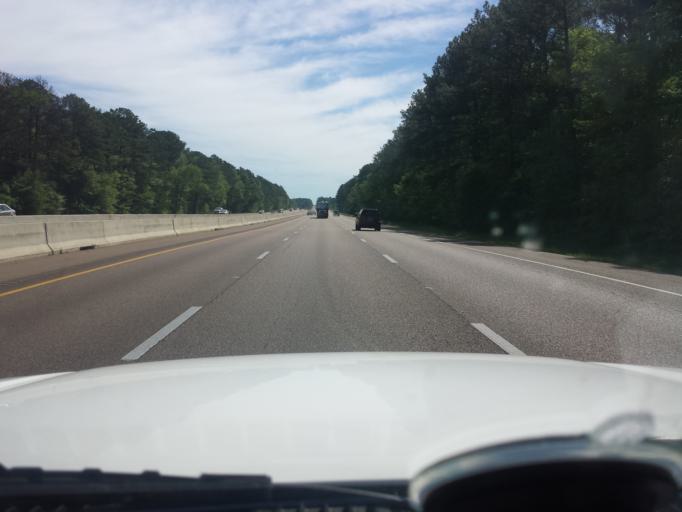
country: US
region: Mississippi
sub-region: Rankin County
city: Pearl
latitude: 32.2663
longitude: -90.1268
